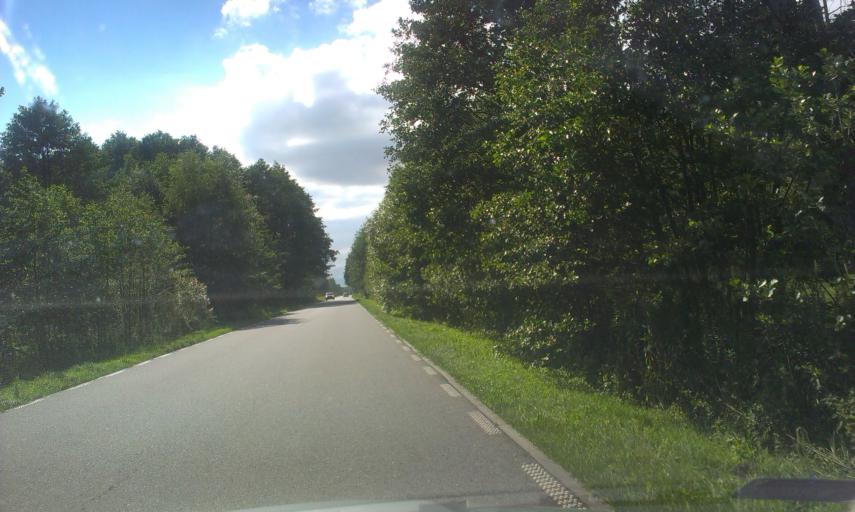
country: PL
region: Lodz Voivodeship
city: Zabia Wola
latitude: 51.9675
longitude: 20.6411
